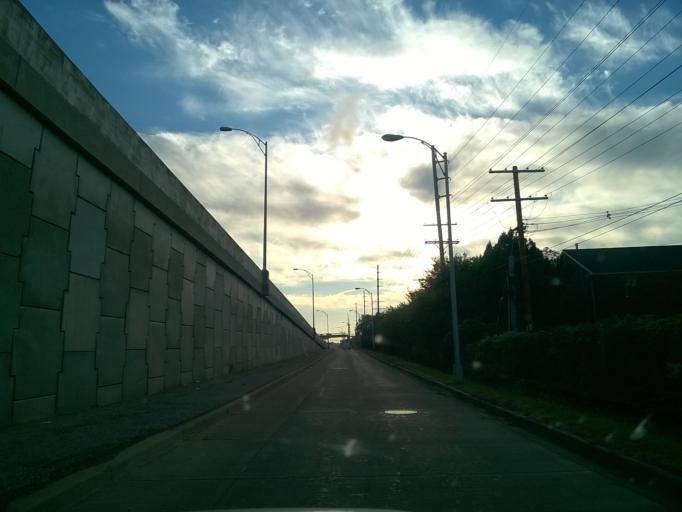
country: US
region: Indiana
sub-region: Vanderburgh County
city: Melody Hill
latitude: 37.9765
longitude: -87.4904
